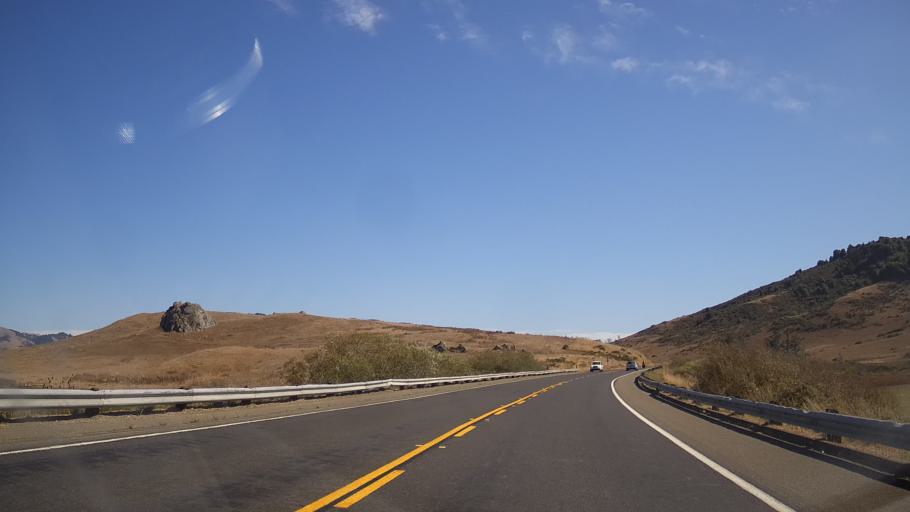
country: US
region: California
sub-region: Marin County
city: Lagunitas-Forest Knolls
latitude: 38.0858
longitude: -122.7231
